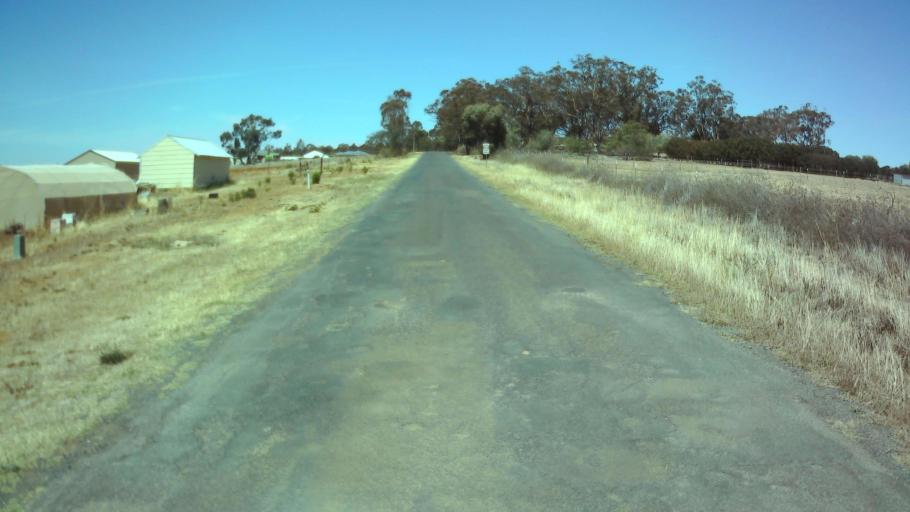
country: AU
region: New South Wales
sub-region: Weddin
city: Grenfell
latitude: -33.9004
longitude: 148.1729
